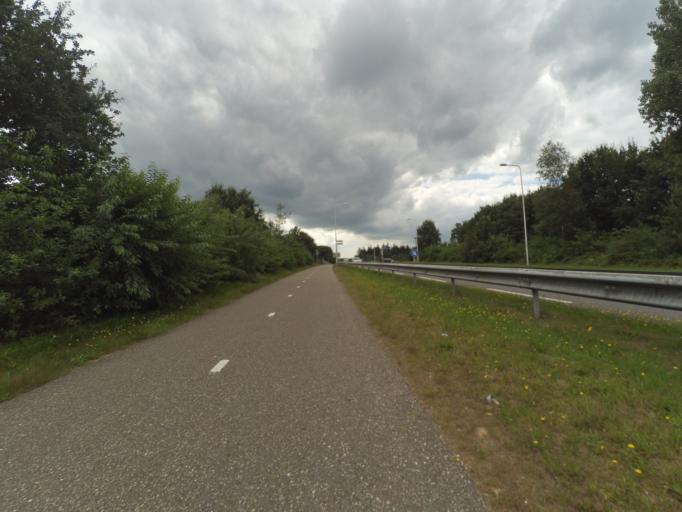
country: NL
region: Utrecht
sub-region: Gemeente Amersfoort
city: Amersfoort
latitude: 52.1304
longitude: 5.3695
